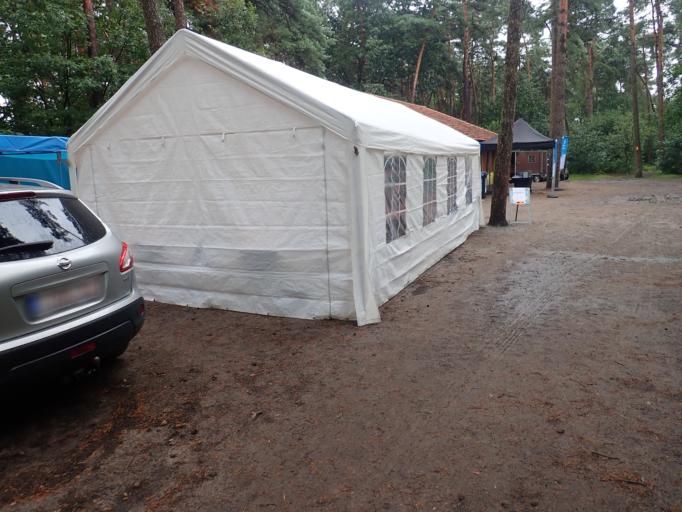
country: BE
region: Flanders
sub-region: Provincie Antwerpen
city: Beerse
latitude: 51.2821
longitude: 4.8345
